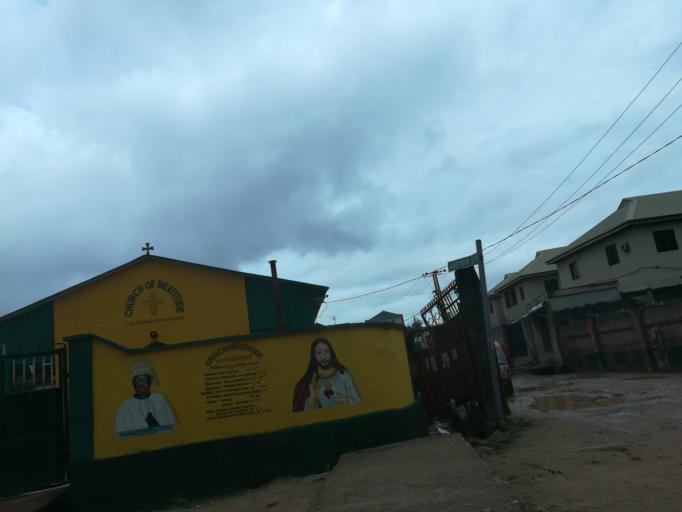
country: NG
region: Lagos
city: Agege
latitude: 6.6128
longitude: 3.3257
